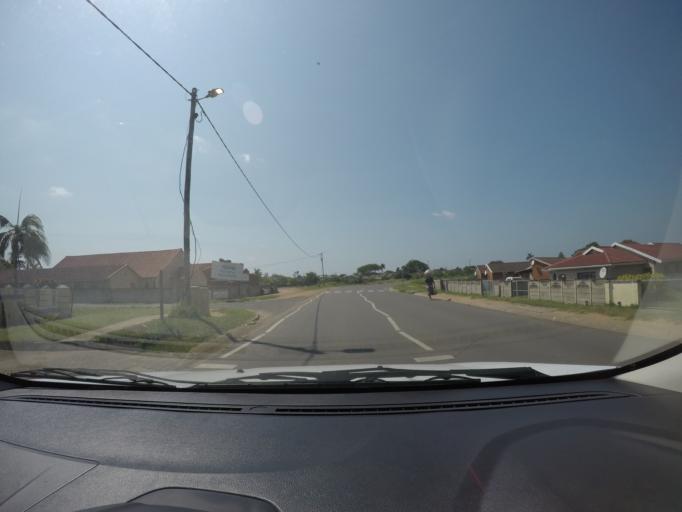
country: ZA
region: KwaZulu-Natal
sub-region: uThungulu District Municipality
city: eSikhawini
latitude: -28.8661
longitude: 31.9110
